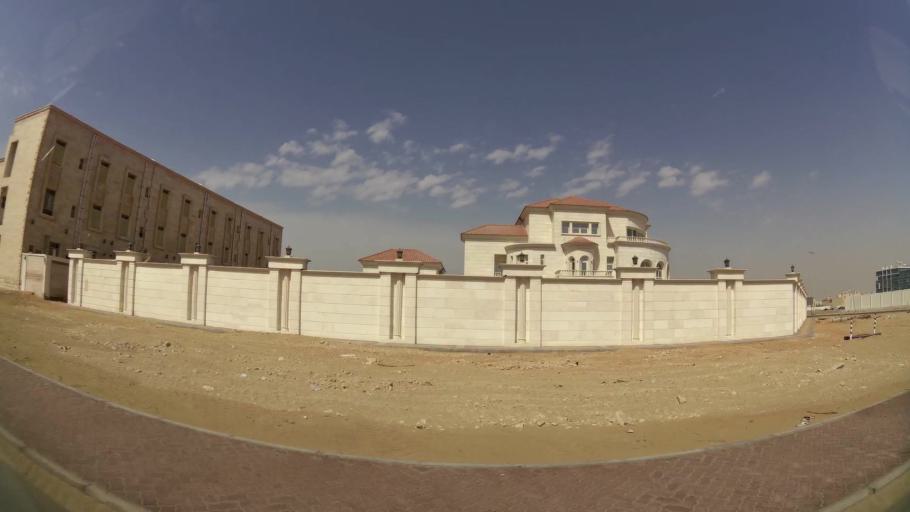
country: AE
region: Abu Dhabi
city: Abu Dhabi
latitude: 24.3161
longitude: 54.5518
